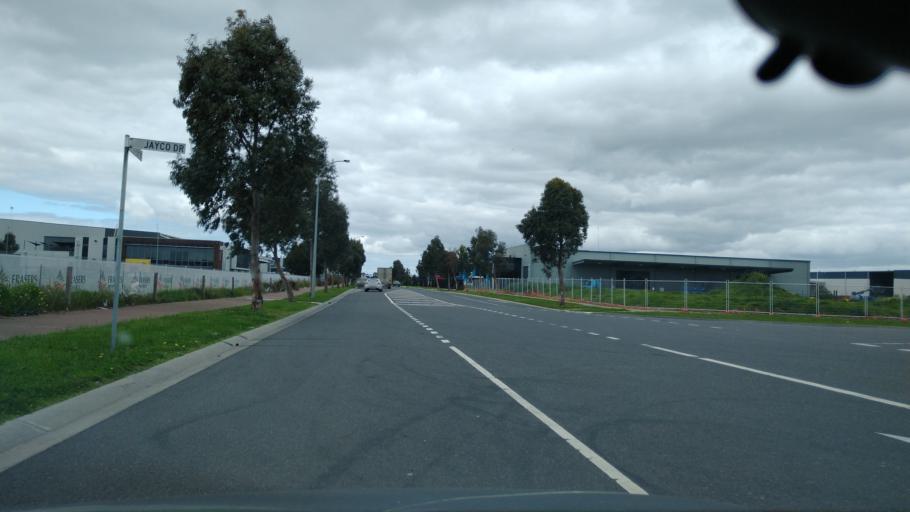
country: AU
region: Victoria
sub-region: Frankston
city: Sandhurst
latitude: -38.0490
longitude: 145.2170
